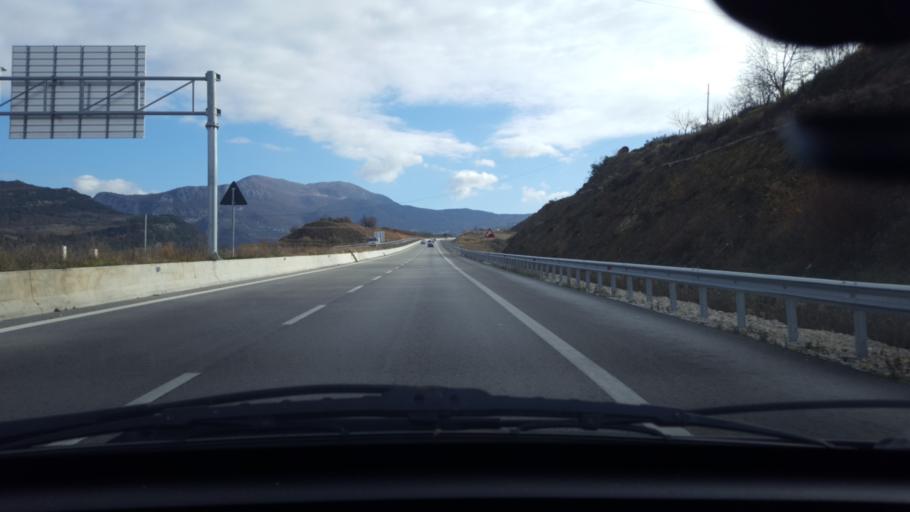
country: AL
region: Tirane
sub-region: Rrethi i Tiranes
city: Krrabe
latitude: 41.2263
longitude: 19.9358
